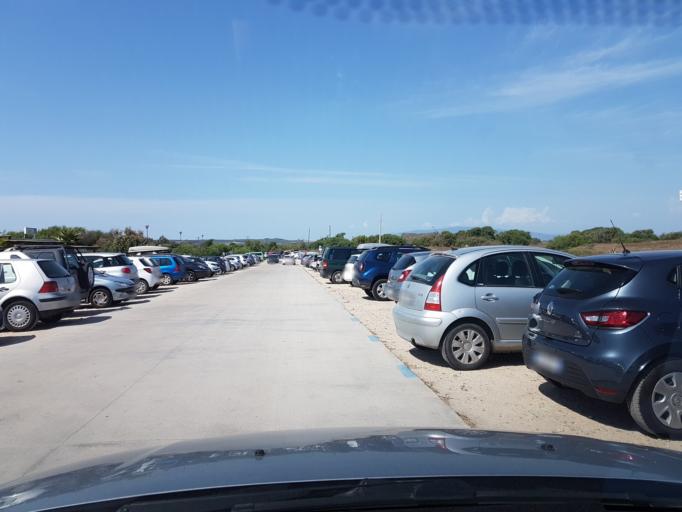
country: IT
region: Sardinia
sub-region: Provincia di Oristano
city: Cabras
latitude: 39.8791
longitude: 8.4393
